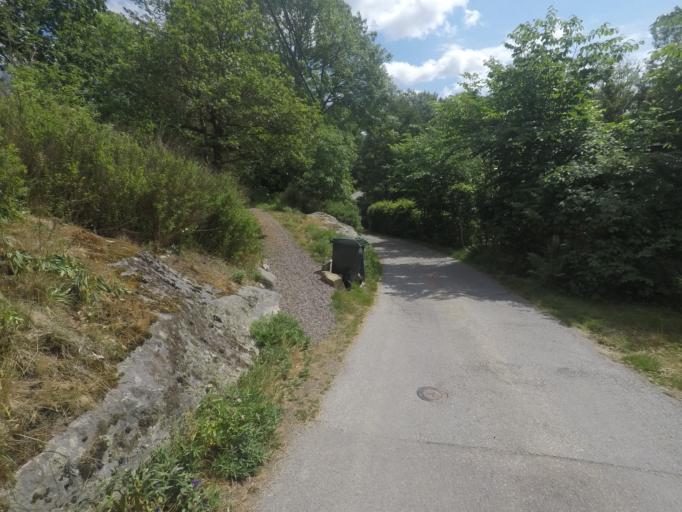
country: SE
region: Vaestra Goetaland
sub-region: Goteborg
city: Billdal
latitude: 57.5776
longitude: 11.9510
